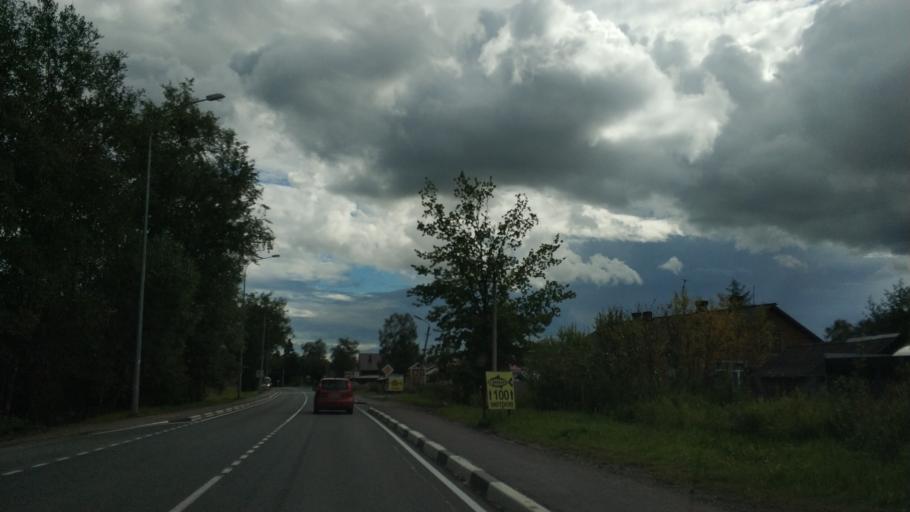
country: RU
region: Republic of Karelia
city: Khelyulya
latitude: 61.7517
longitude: 30.6608
